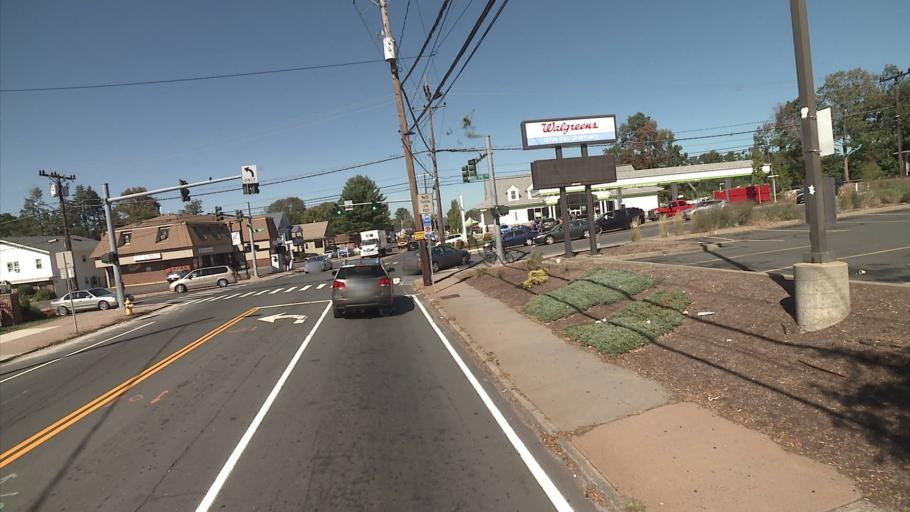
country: US
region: Connecticut
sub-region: Hartford County
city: Manchester
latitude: 41.7831
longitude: -72.5231
